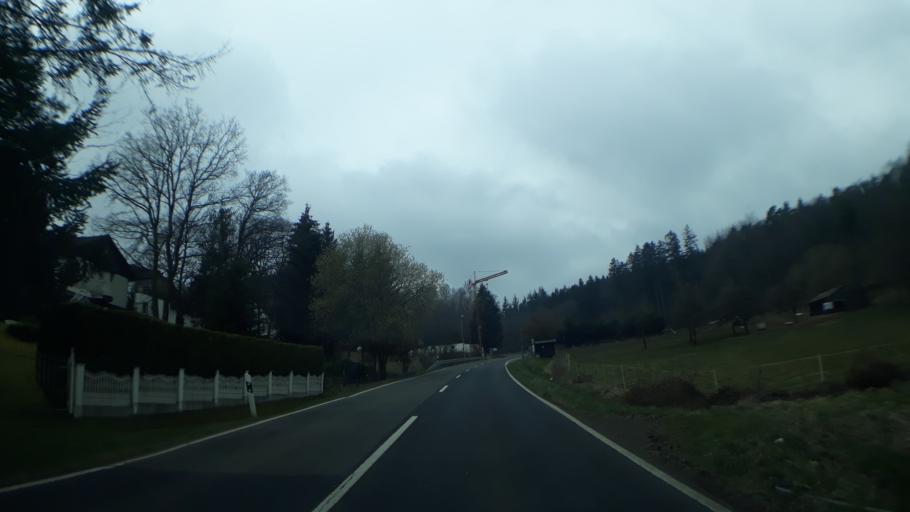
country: DE
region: North Rhine-Westphalia
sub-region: Regierungsbezirk Koln
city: Kall
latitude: 50.5269
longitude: 6.5249
